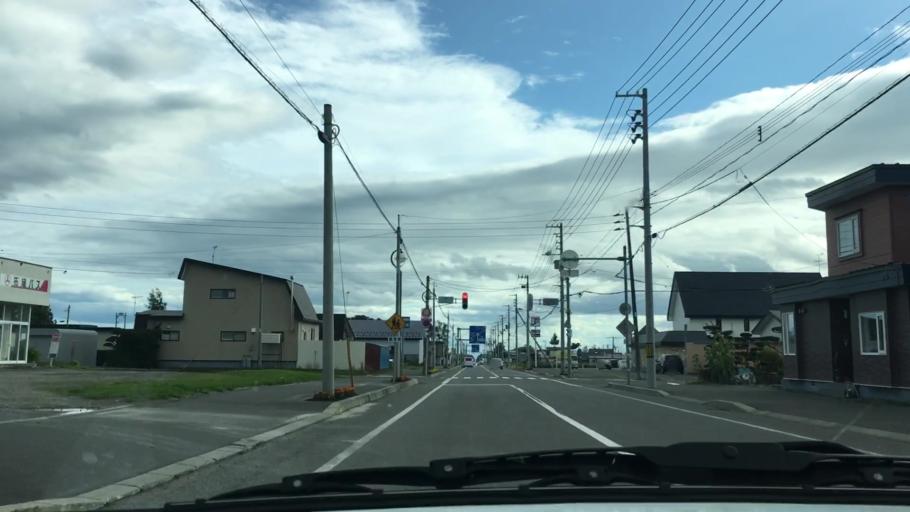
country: JP
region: Hokkaido
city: Otofuke
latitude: 43.2298
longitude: 143.2944
